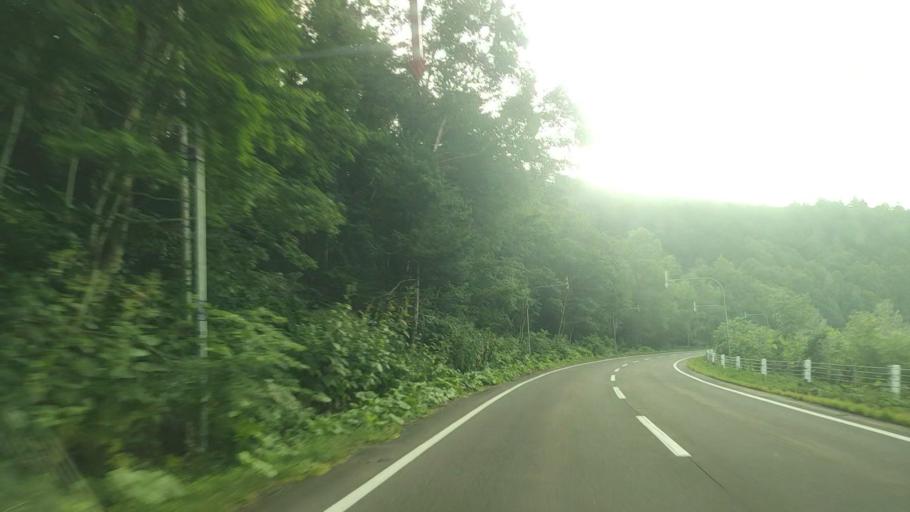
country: JP
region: Hokkaido
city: Bibai
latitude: 43.1289
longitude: 142.0980
